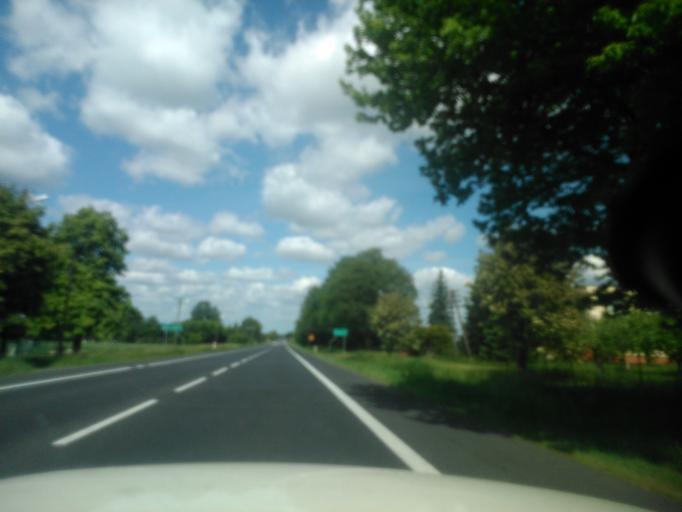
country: PL
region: Kujawsko-Pomorskie
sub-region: Powiat torunski
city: Obrowo
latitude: 53.0088
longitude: 18.8335
